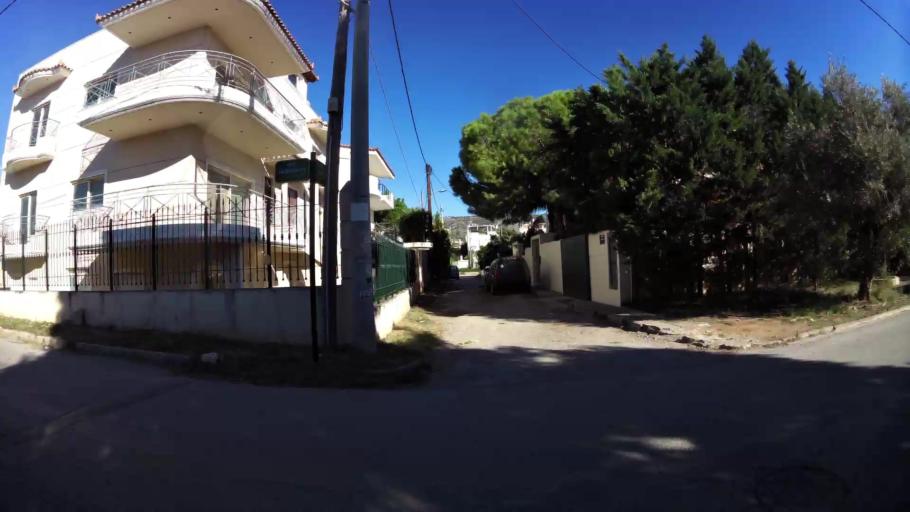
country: GR
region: Attica
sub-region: Nomarchia Anatolikis Attikis
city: Vari
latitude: 37.8359
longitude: 23.8140
